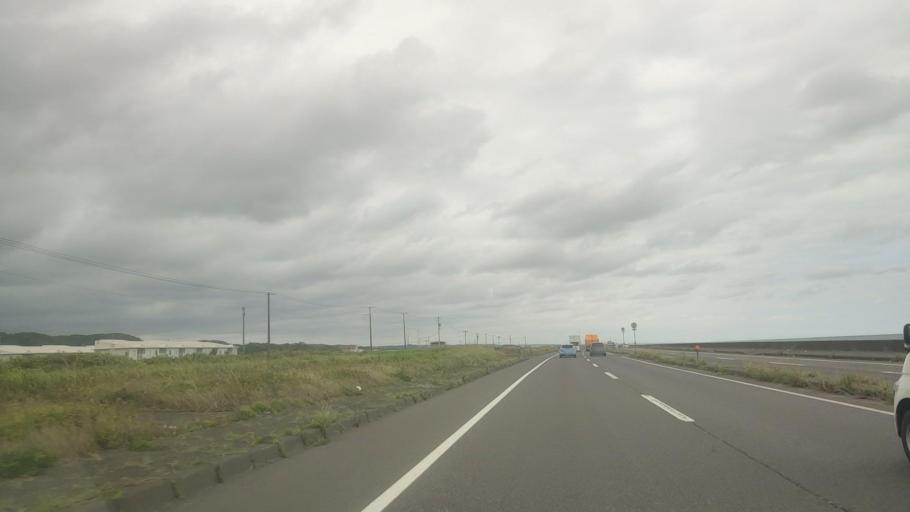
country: JP
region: Hokkaido
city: Shiraoi
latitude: 42.5532
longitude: 141.3706
